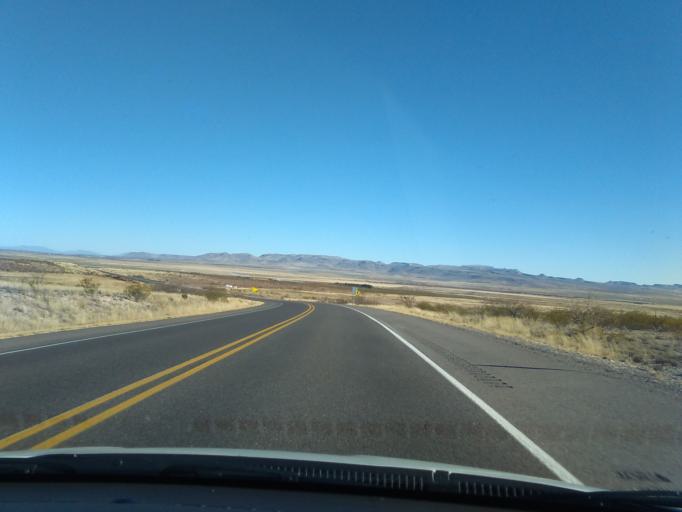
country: US
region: New Mexico
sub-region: Dona Ana County
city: Hatch
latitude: 32.5735
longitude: -107.4071
